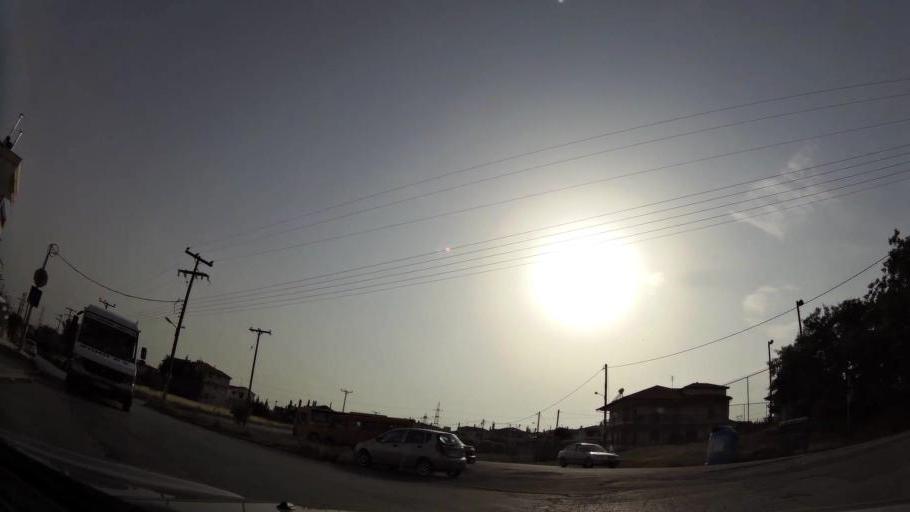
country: GR
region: Central Macedonia
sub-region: Nomos Thessalonikis
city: Oraiokastro
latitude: 40.7214
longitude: 22.9054
